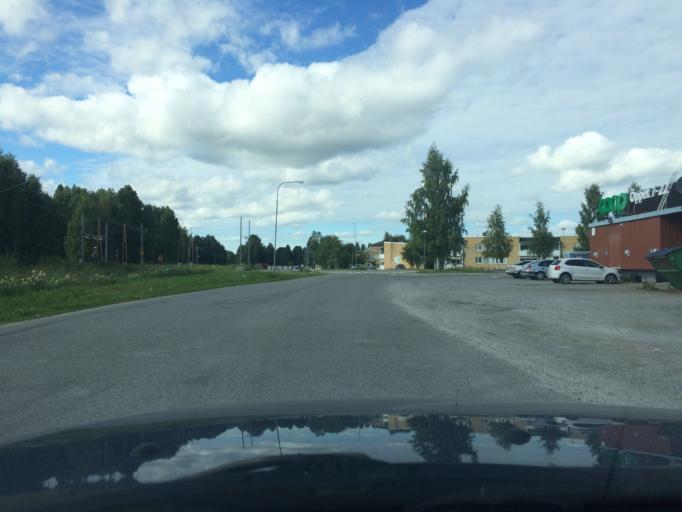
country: SE
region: Norrbotten
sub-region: Pitea Kommun
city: Bergsviken
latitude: 65.3418
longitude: 21.3945
